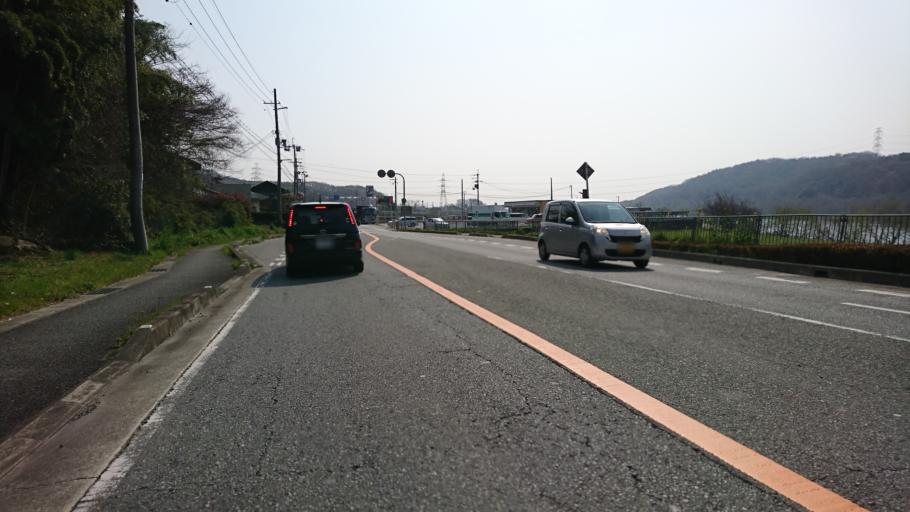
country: JP
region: Hyogo
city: Ono
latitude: 34.8111
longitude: 134.9316
